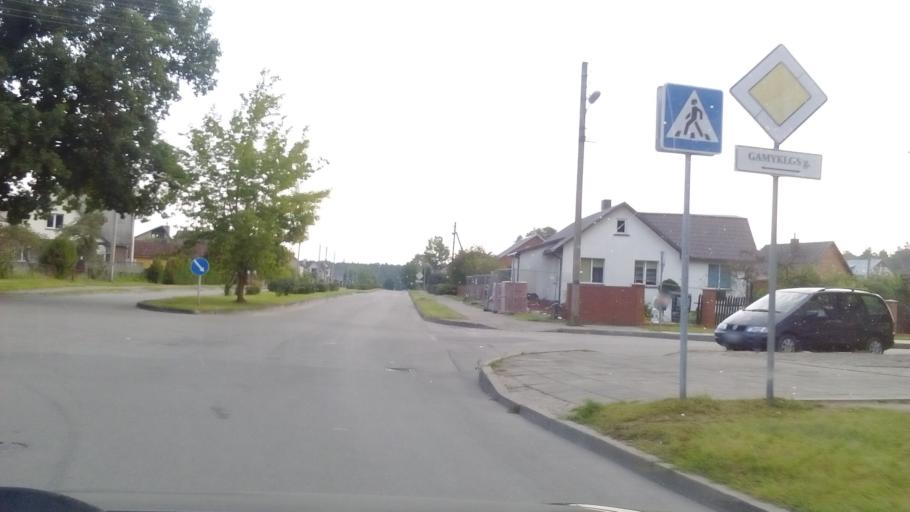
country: LT
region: Alytaus apskritis
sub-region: Alytus
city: Alytus
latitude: 54.3850
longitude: 24.0572
